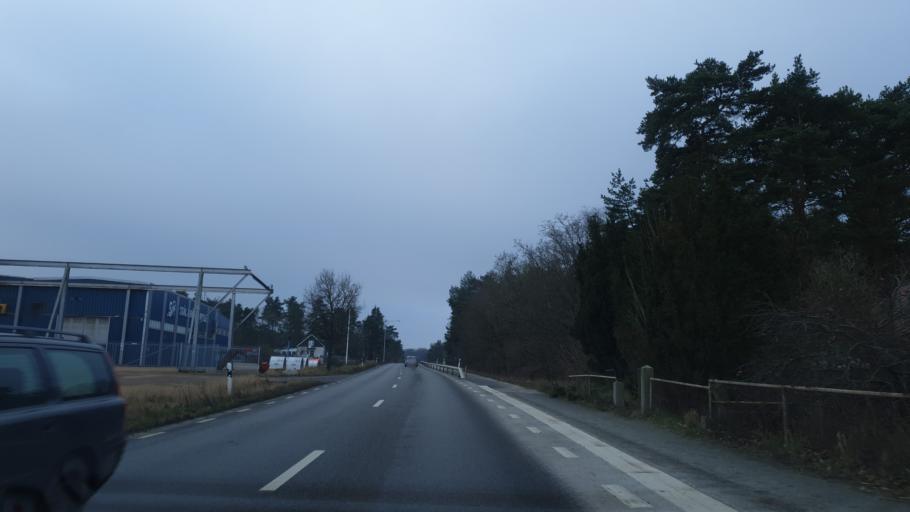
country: SE
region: Blekinge
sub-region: Solvesborgs Kommun
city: Soelvesborg
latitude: 56.1013
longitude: 14.6662
